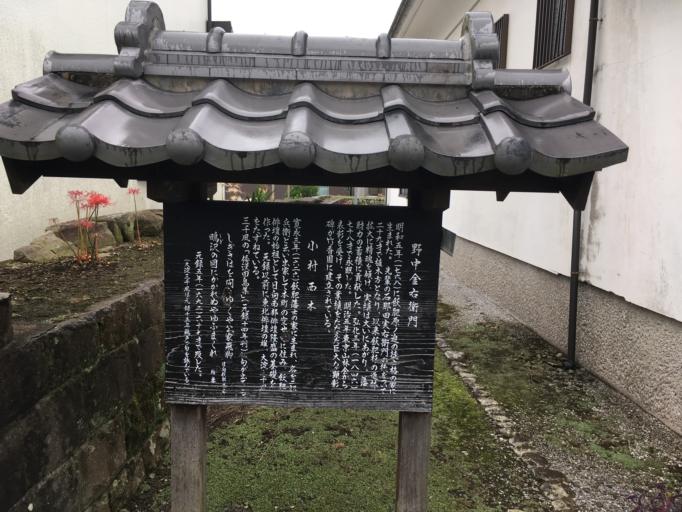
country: JP
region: Miyazaki
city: Nichinan
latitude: 31.6246
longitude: 131.3506
